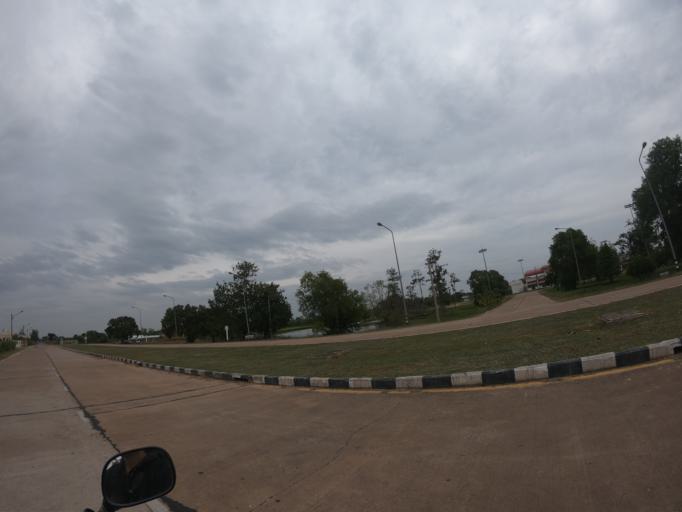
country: TH
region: Roi Et
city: Selaphum
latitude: 16.1440
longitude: 103.8803
